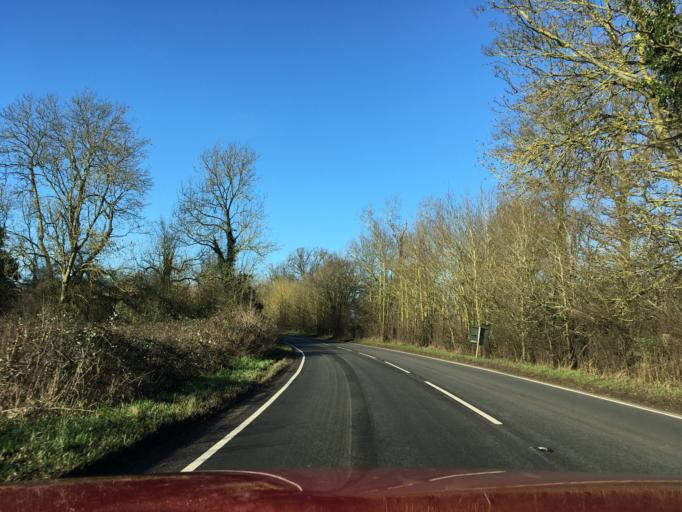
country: GB
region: England
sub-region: Warwickshire
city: Wellesbourne Mountford
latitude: 52.1998
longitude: -1.6221
